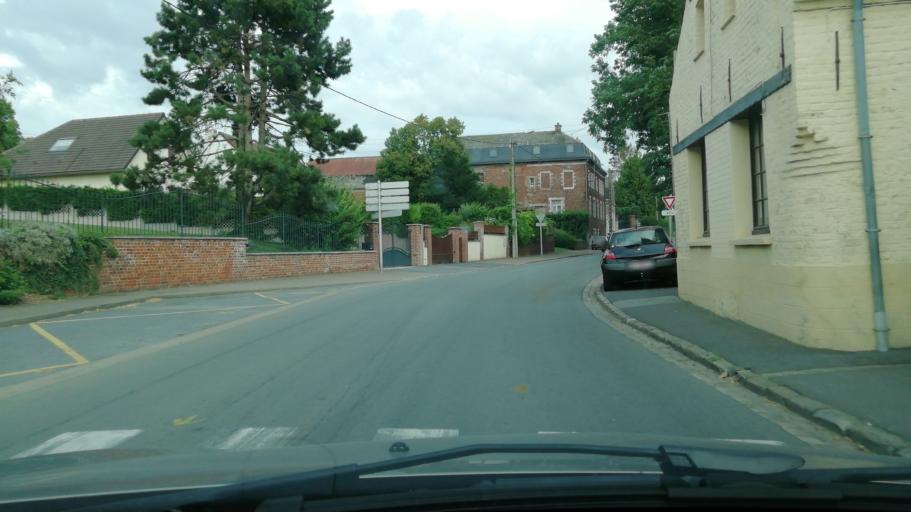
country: FR
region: Nord-Pas-de-Calais
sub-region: Departement du Nord
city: Rieux-en-Cambresis
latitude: 50.1663
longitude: 3.3466
